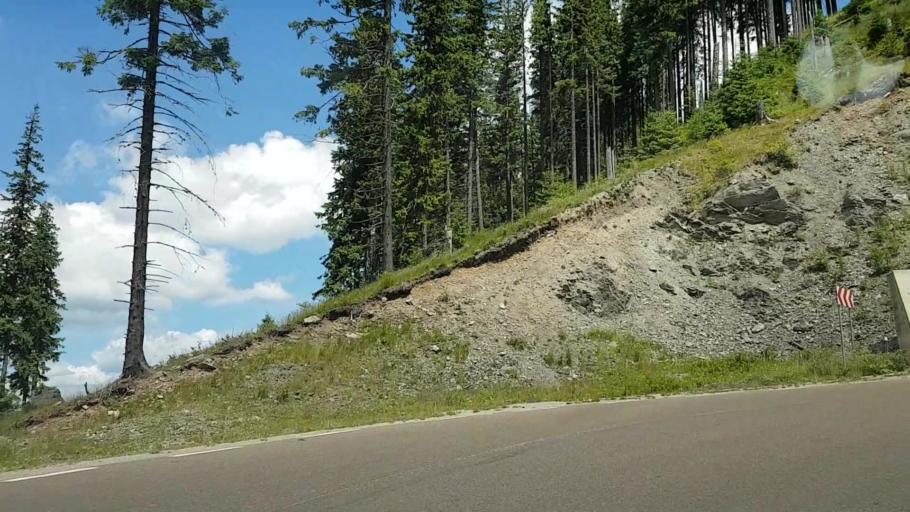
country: RO
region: Suceava
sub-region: Comuna Sadova
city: Sadova
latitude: 47.4595
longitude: 25.5251
